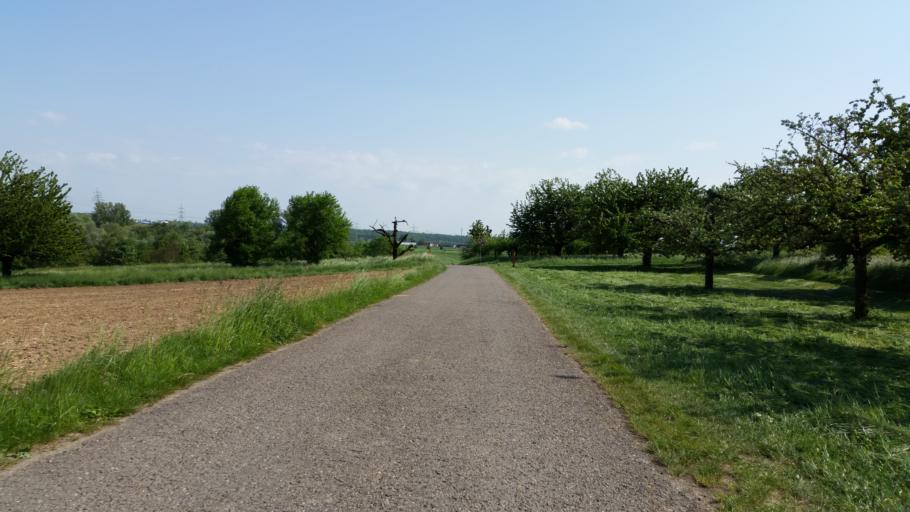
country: DE
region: Baden-Wuerttemberg
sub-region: Regierungsbezirk Stuttgart
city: Pleidelsheim
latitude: 48.9782
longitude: 9.2081
